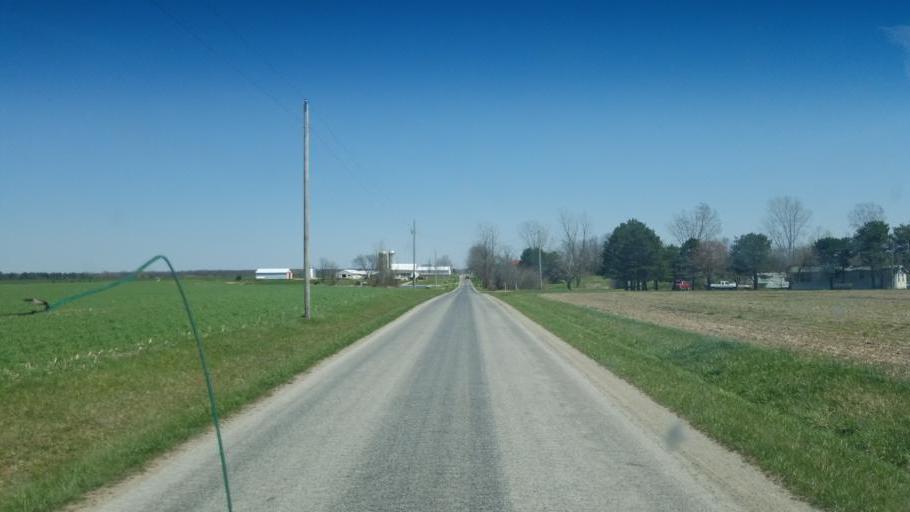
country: US
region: Ohio
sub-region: Huron County
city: Greenwich
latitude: 41.0472
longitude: -82.4671
